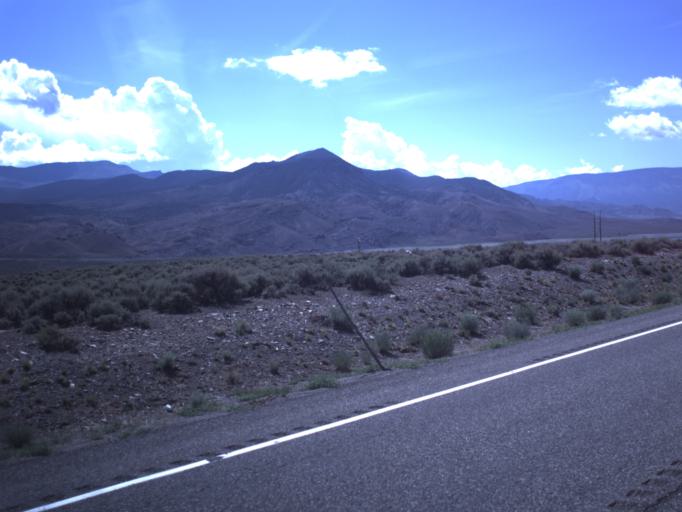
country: US
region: Utah
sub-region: Piute County
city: Junction
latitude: 38.3360
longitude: -112.2176
